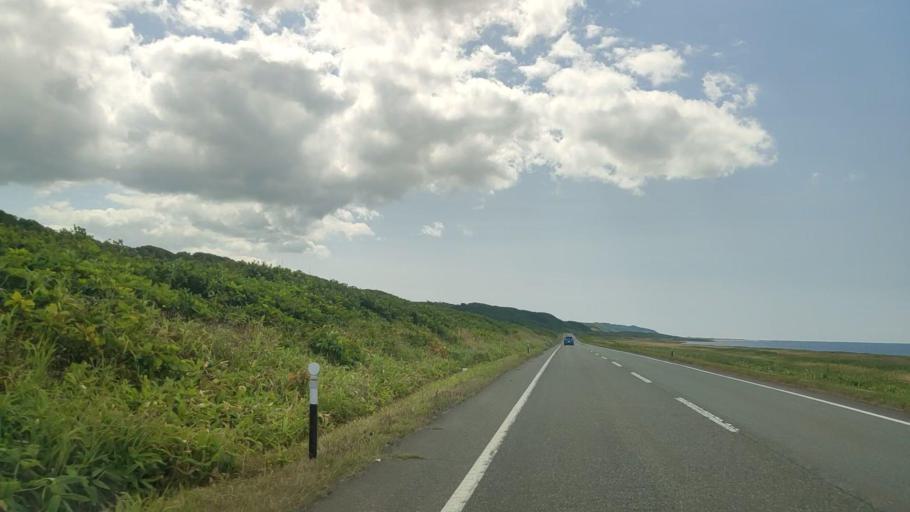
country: JP
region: Hokkaido
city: Wakkanai
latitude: 45.2790
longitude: 141.6159
